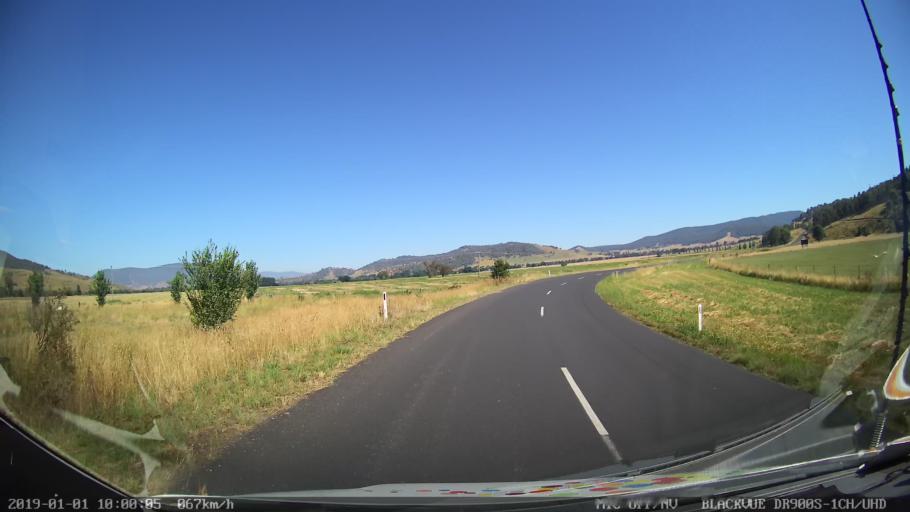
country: AU
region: New South Wales
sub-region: Snowy River
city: Jindabyne
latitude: -36.2061
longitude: 148.1024
